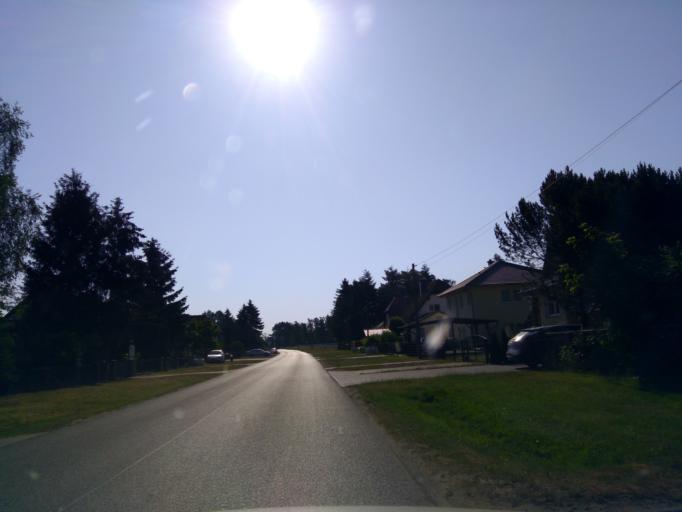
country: DE
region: Brandenburg
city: Brieselang
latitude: 52.5605
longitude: 13.0249
